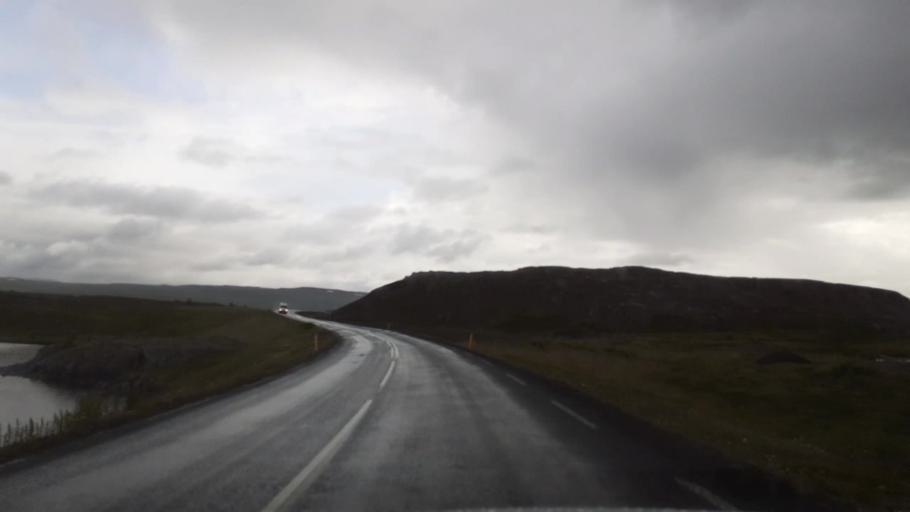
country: IS
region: East
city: Egilsstadir
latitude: 65.2999
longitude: -14.4568
